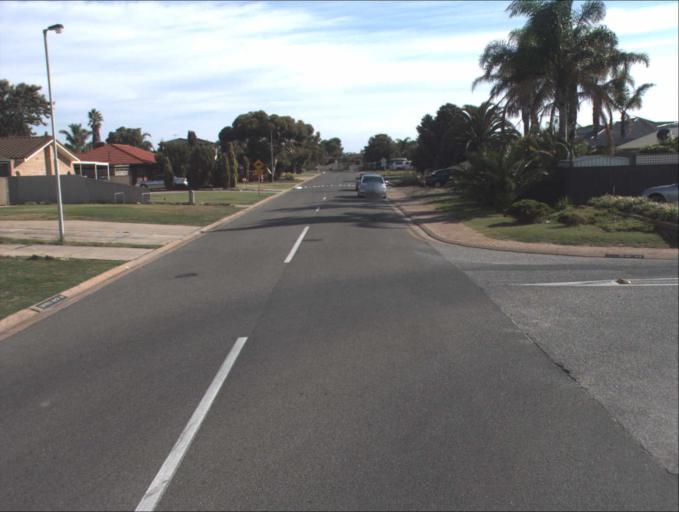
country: AU
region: South Australia
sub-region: Port Adelaide Enfield
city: Birkenhead
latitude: -34.7910
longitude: 138.4954
